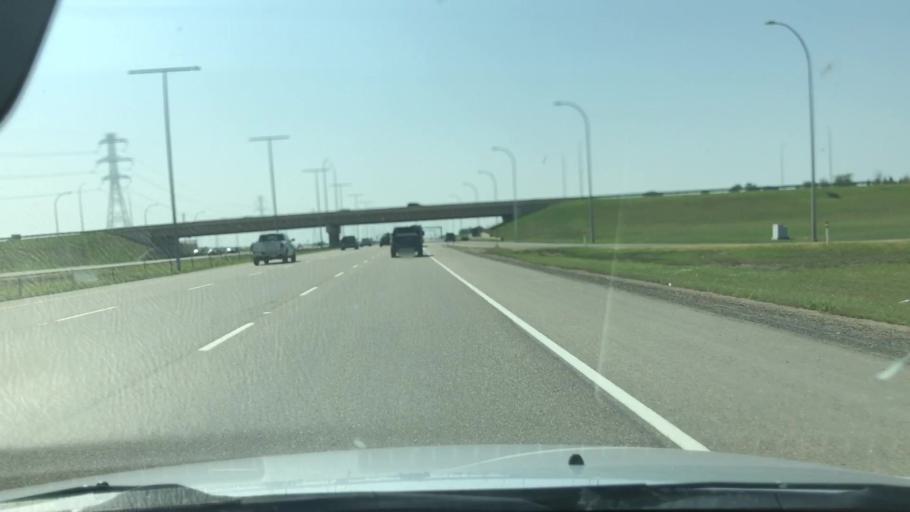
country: CA
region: Alberta
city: St. Albert
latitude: 53.5248
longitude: -113.6595
